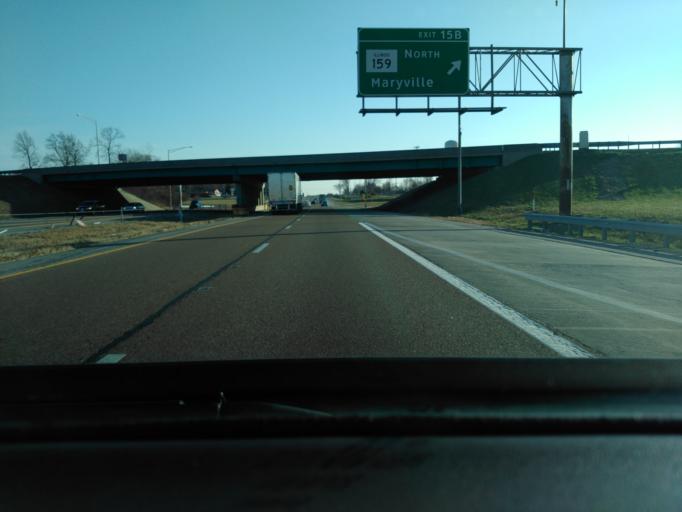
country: US
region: Illinois
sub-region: Madison County
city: Maryville
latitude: 38.7078
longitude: -89.9599
